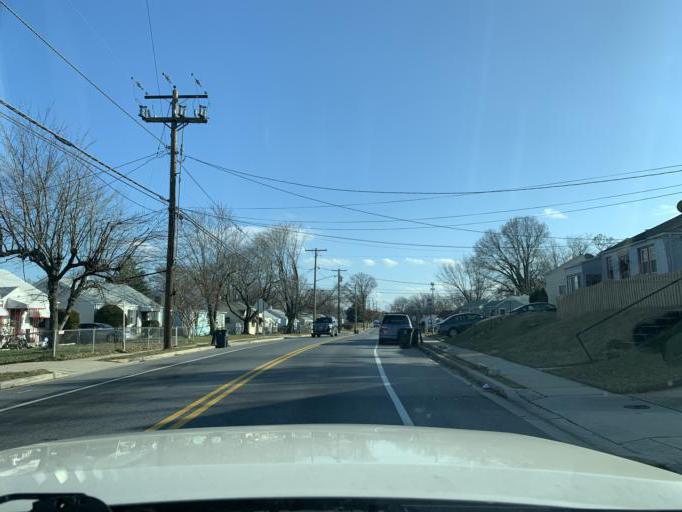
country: US
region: Maryland
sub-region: Prince George's County
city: Fairmount Heights
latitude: 38.9095
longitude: -76.9214
